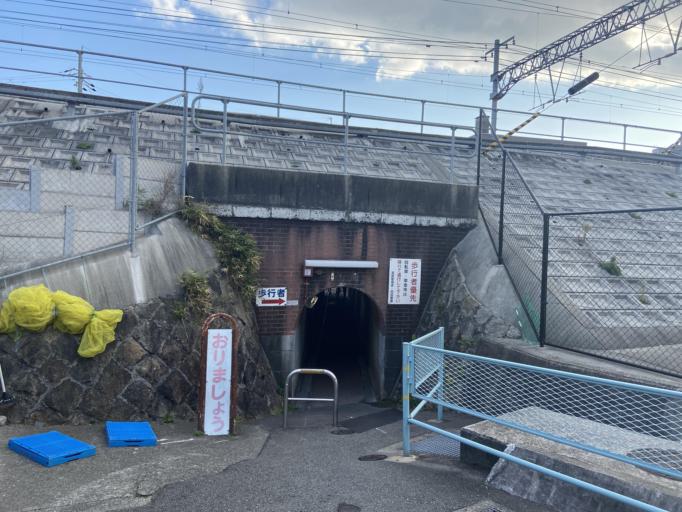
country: JP
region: Hyogo
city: Ashiya
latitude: 34.7374
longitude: 135.3208
